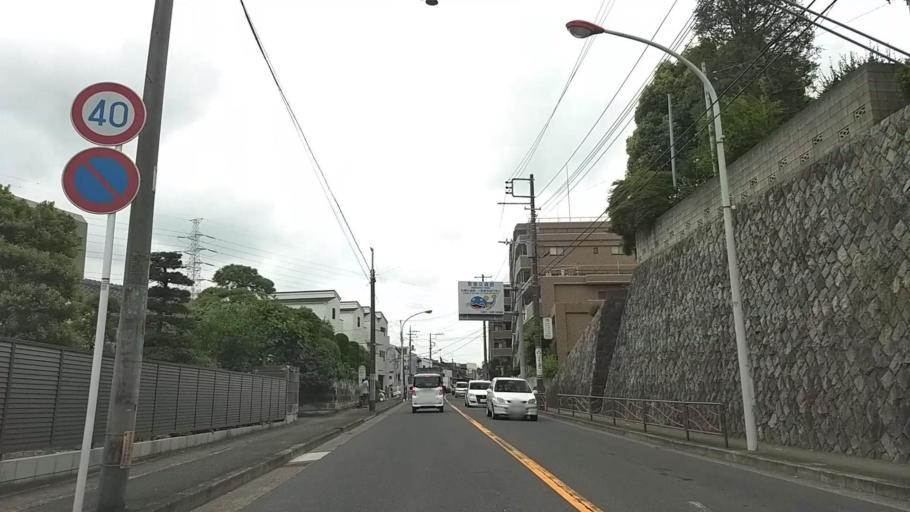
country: JP
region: Tokyo
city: Chofugaoka
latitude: 35.5706
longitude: 139.6161
